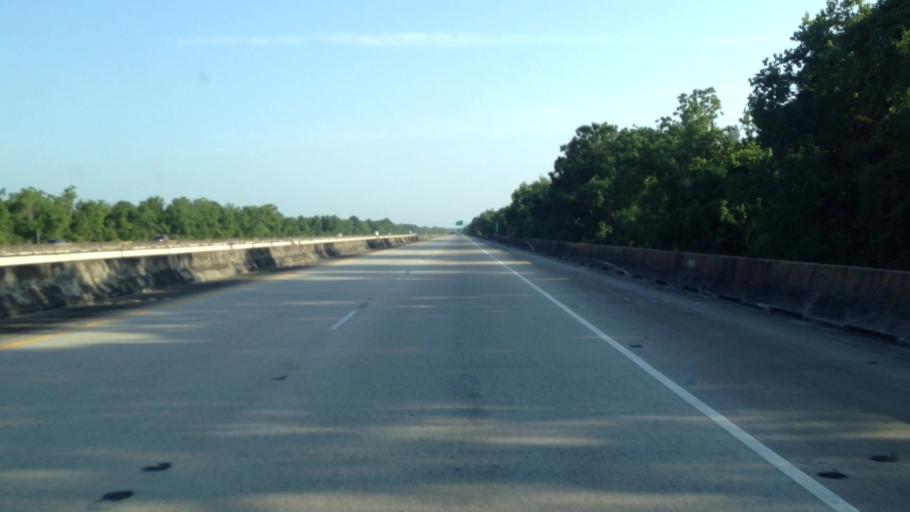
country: US
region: Louisiana
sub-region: Tangipahoa Parish
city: Ponchatoula
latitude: 30.3767
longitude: -90.4239
